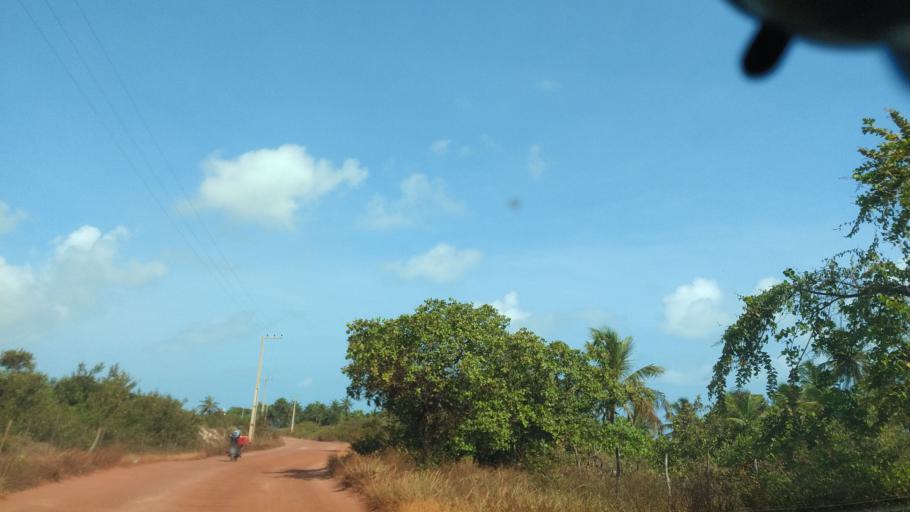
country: BR
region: Rio Grande do Norte
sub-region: Touros
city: Touros
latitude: -5.1585
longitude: -35.4970
